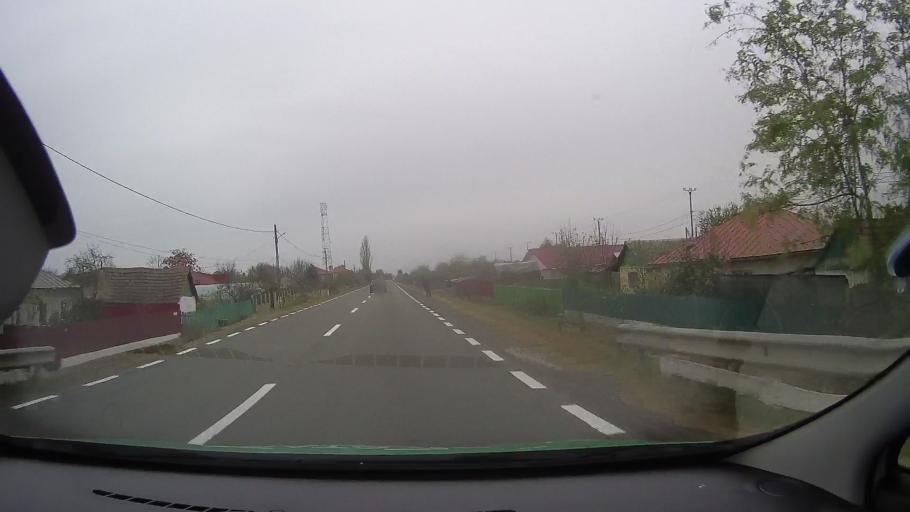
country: RO
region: Ialomita
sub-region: Comuna Giurgeni
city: Giurgeni
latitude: 44.7490
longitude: 27.8571
